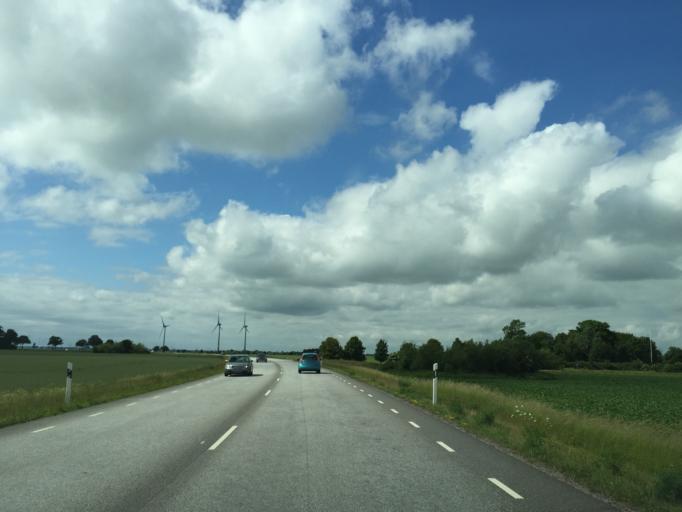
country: SE
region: Skane
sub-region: Staffanstorps Kommun
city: Hjaerup
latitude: 55.6912
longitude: 13.1489
